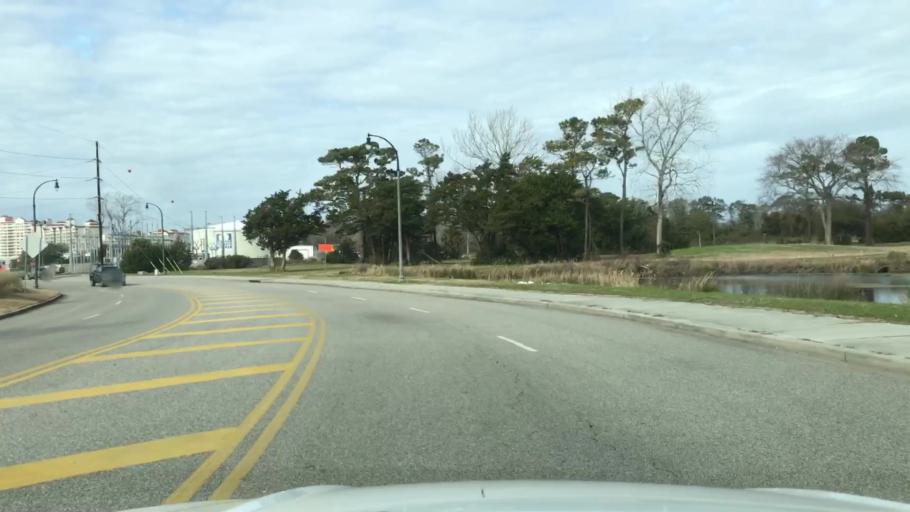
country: US
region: South Carolina
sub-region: Horry County
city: North Myrtle Beach
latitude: 33.8006
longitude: -78.7372
